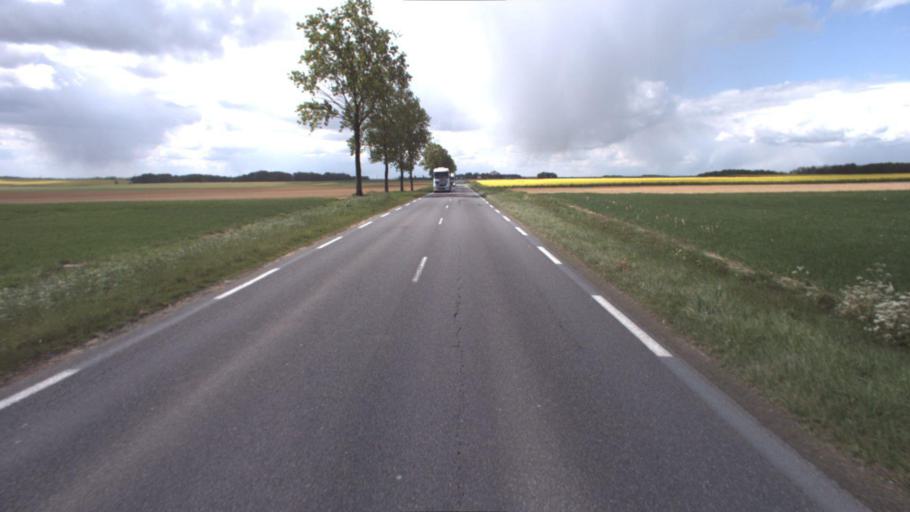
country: FR
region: Ile-de-France
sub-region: Departement de Seine-et-Marne
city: Choisy-en-Brie
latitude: 48.6926
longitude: 3.1978
